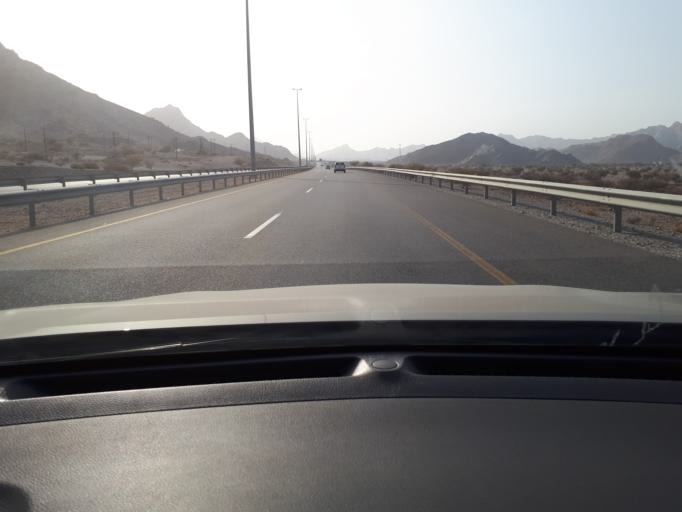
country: OM
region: Muhafazat Masqat
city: Muscat
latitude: 23.3519
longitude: 58.6869
